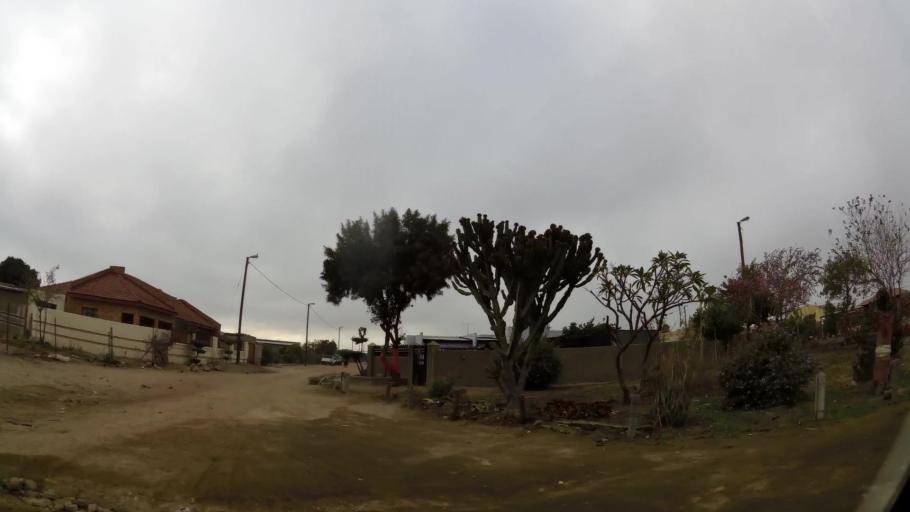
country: ZA
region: Limpopo
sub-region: Capricorn District Municipality
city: Polokwane
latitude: -23.8347
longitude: 29.3892
